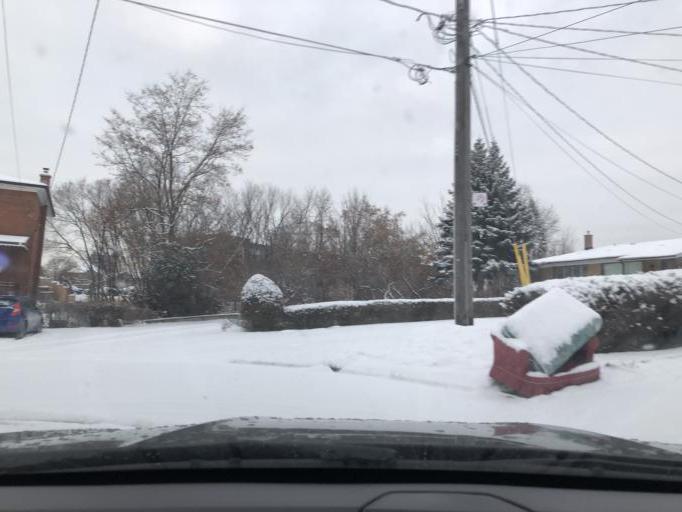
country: CA
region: Ontario
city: Toronto
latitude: 43.7009
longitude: -79.4779
